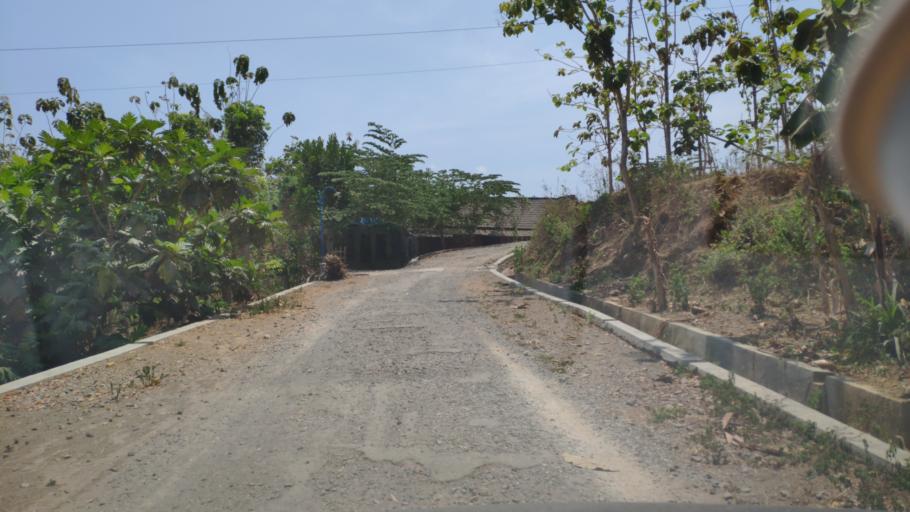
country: ID
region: Central Java
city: Banyubang
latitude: -6.9516
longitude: 111.5231
